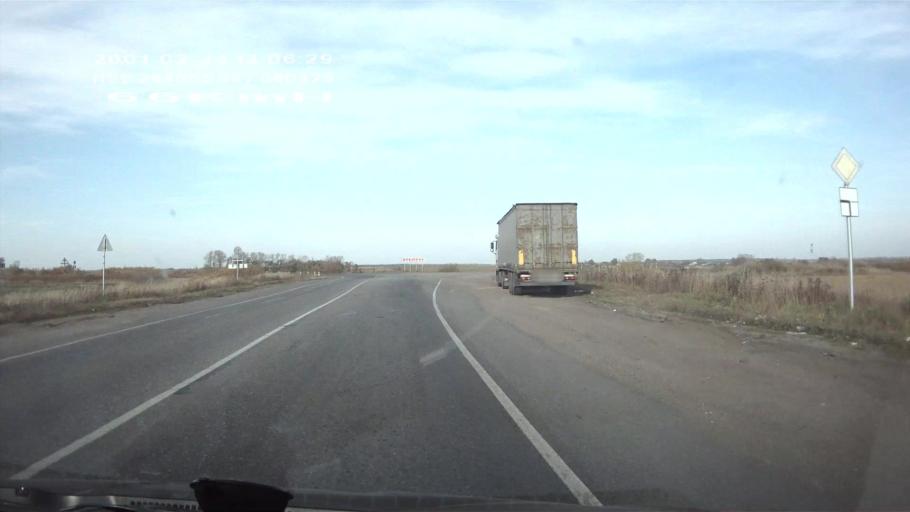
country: RU
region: Chuvashia
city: Ibresi
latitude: 55.2847
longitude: 47.0802
